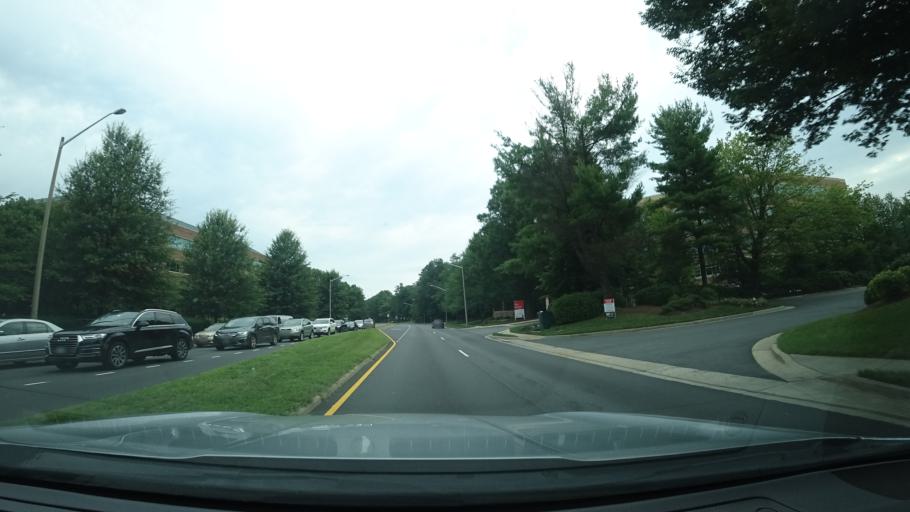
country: US
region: Virginia
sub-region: Fairfax County
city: Reston
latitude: 38.9521
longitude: -77.3351
